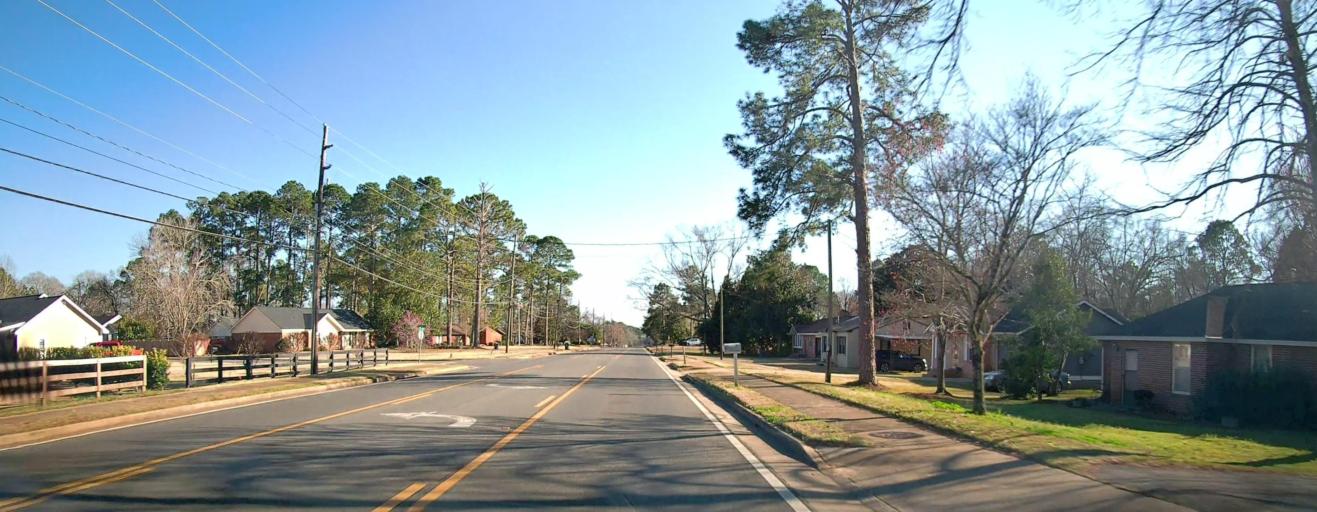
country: US
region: Georgia
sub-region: Sumter County
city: Americus
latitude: 32.0501
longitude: -84.2247
